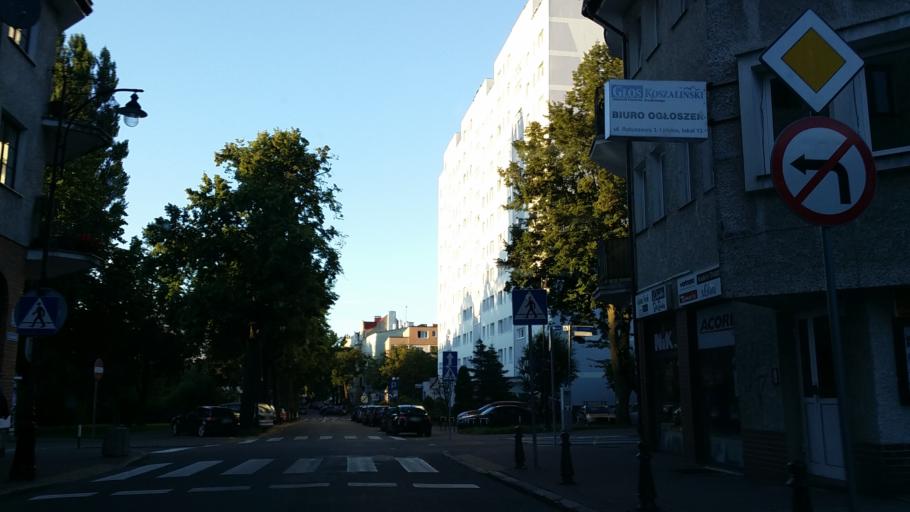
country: PL
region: West Pomeranian Voivodeship
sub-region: Powiat kolobrzeski
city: Kolobrzeg
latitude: 54.1770
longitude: 15.5769
